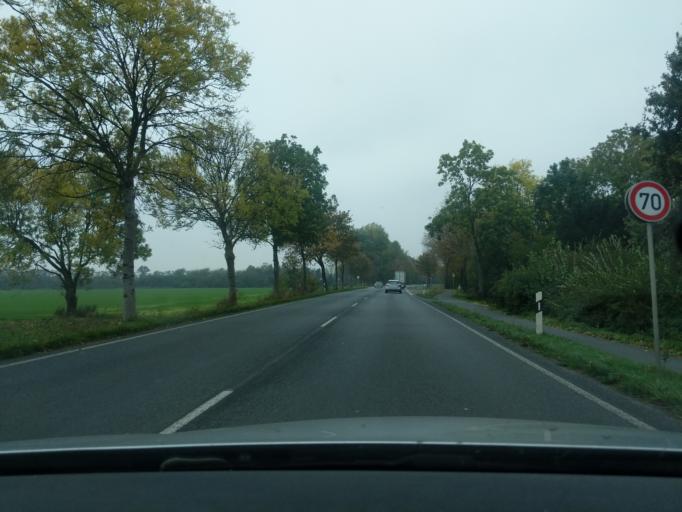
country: DE
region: Lower Saxony
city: Cuxhaven
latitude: 53.8317
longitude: 8.7431
